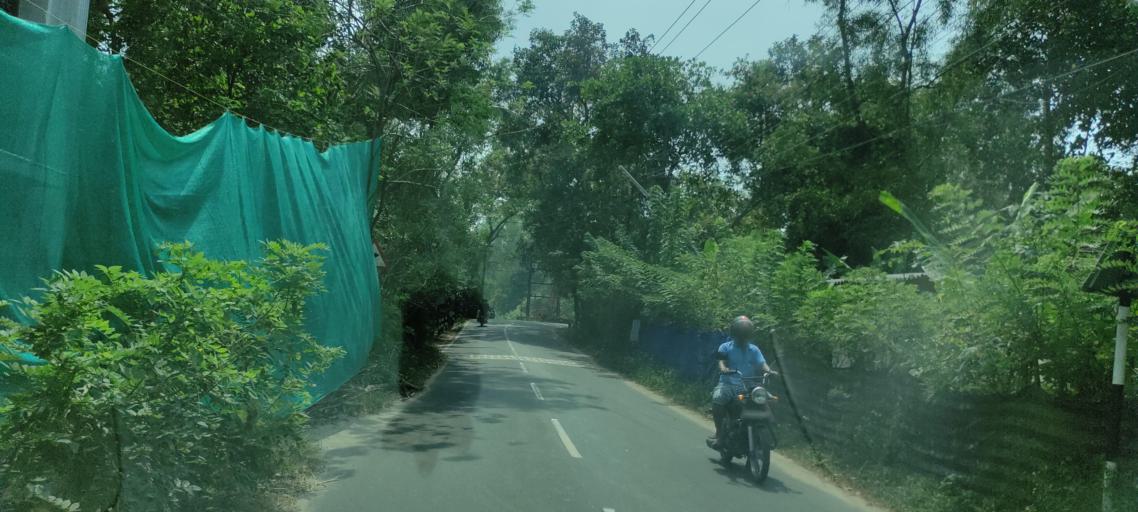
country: IN
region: Kerala
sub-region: Alappuzha
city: Alleppey
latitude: 9.5473
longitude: 76.3327
